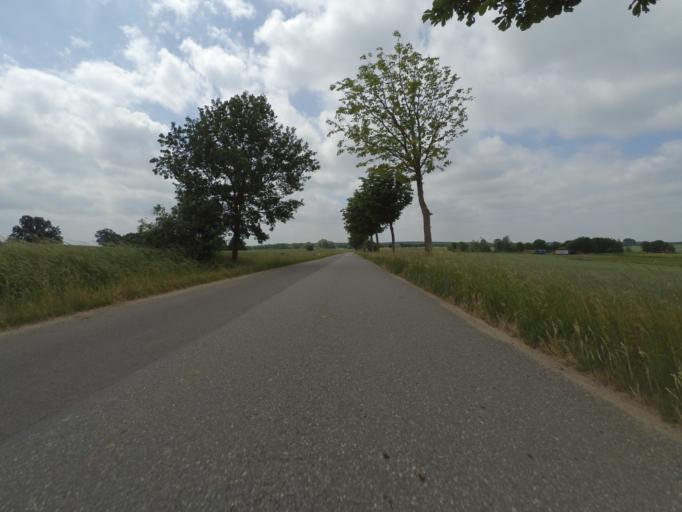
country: DE
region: Mecklenburg-Vorpommern
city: Klink
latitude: 53.4735
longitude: 12.5987
